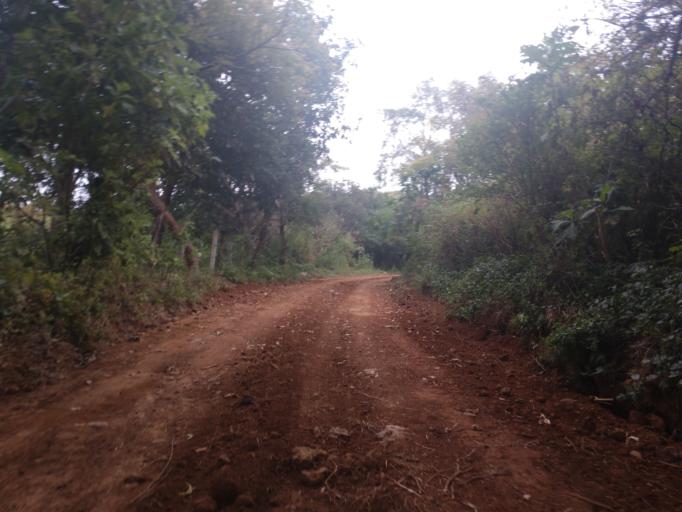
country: MX
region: Nayarit
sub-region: Tepic
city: La Corregidora
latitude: 21.4699
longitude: -104.7905
